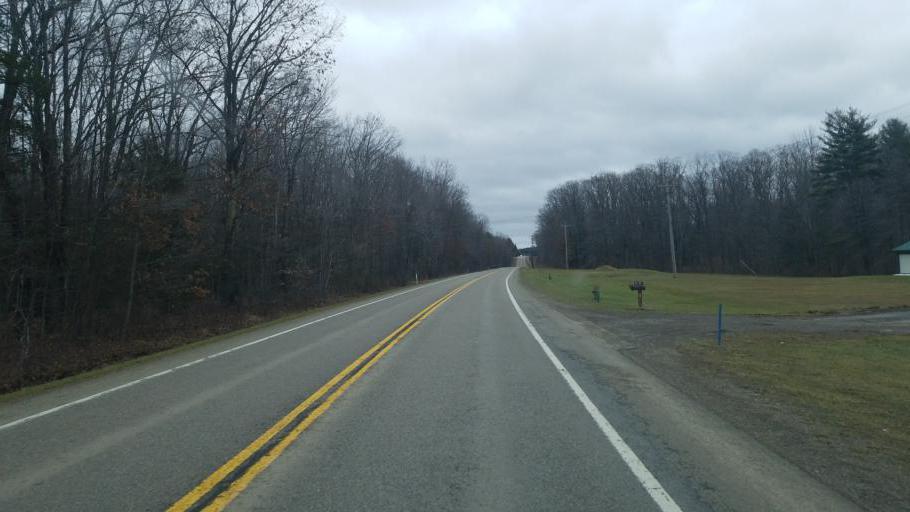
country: US
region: Pennsylvania
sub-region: Forest County
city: Marienville
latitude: 41.4014
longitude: -79.2525
